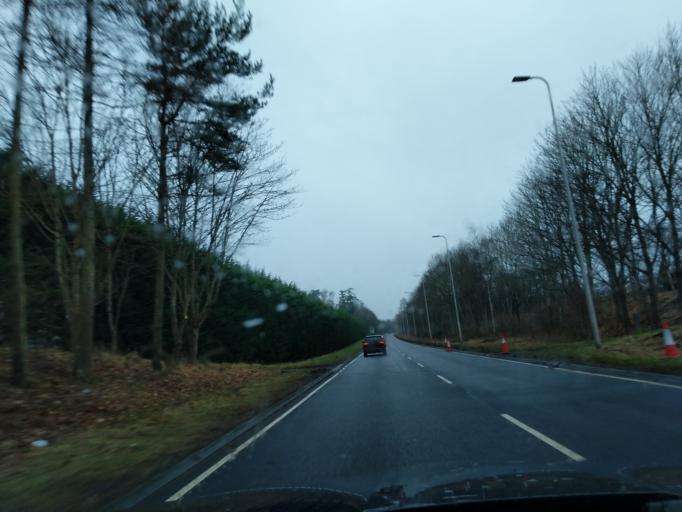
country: GB
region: Scotland
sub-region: The Scottish Borders
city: Melrose
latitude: 55.5966
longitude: -2.7296
